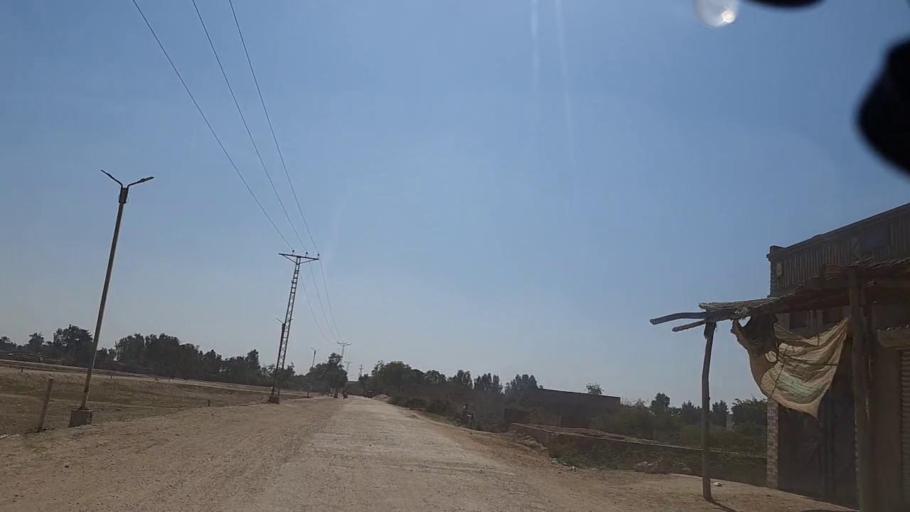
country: PK
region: Sindh
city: Mirpur Khas
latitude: 25.5082
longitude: 69.0300
